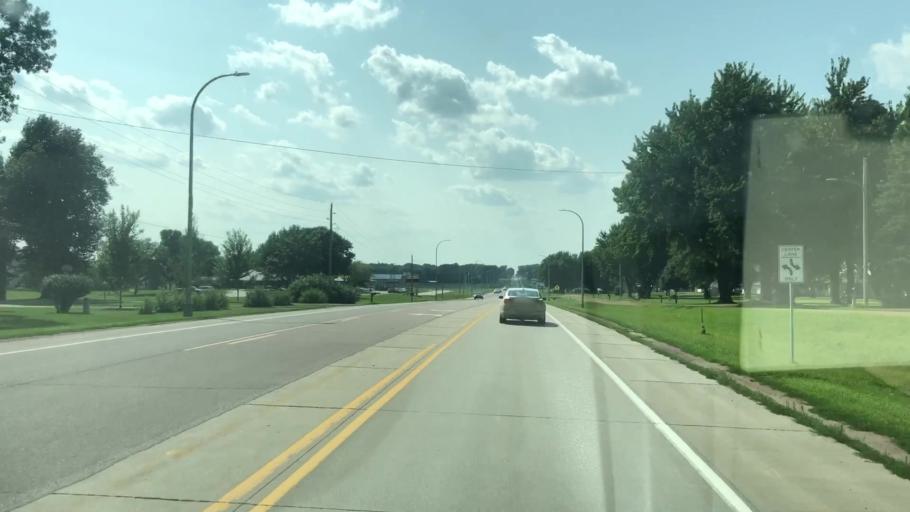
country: US
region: Iowa
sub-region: O'Brien County
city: Sheldon
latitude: 43.1861
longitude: -95.8232
